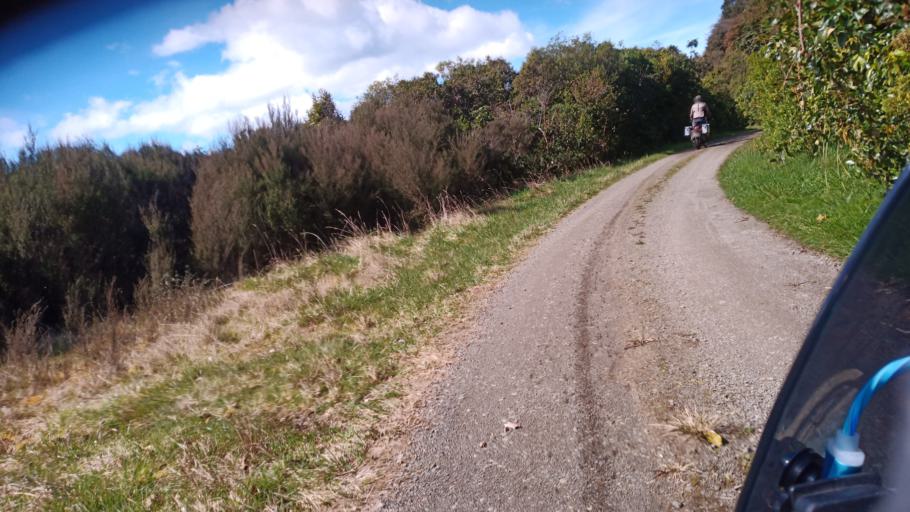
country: NZ
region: Hawke's Bay
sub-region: Wairoa District
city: Wairoa
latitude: -38.7999
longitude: 177.1179
